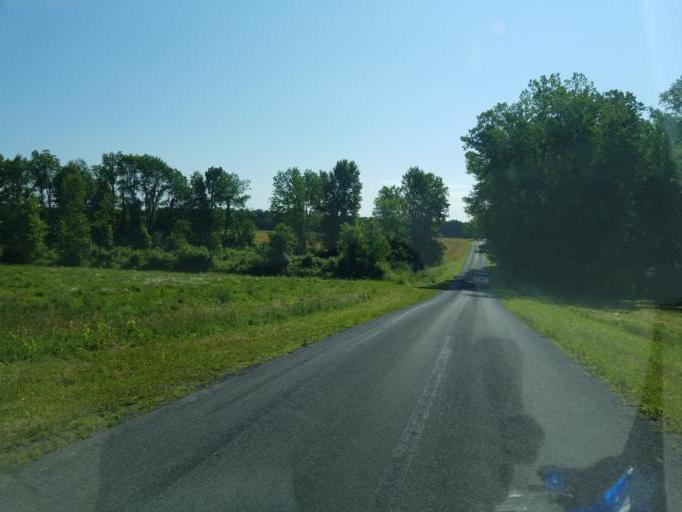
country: US
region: New York
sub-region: Wayne County
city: Clyde
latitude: 43.0545
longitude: -76.8958
